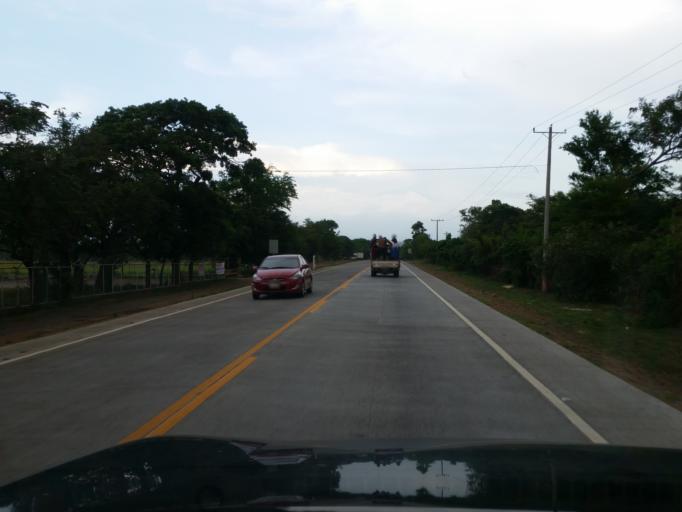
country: NI
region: Managua
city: Carlos Fonseca Amador
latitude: 12.0710
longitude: -86.4895
